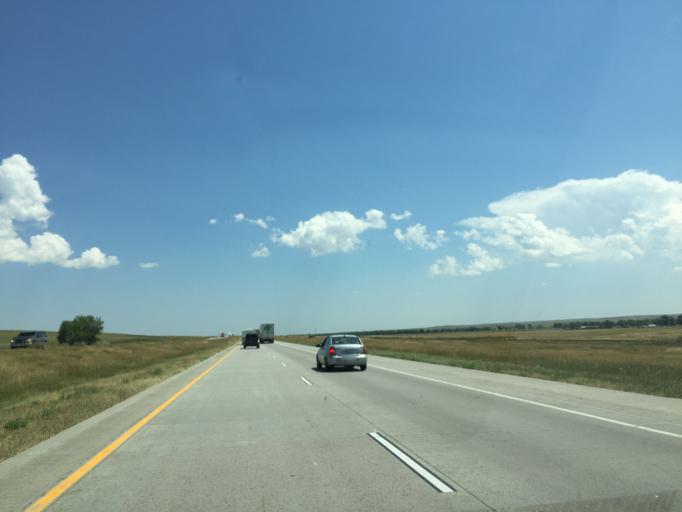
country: US
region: Colorado
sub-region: Lincoln County
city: Limon
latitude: 39.2953
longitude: -103.8026
